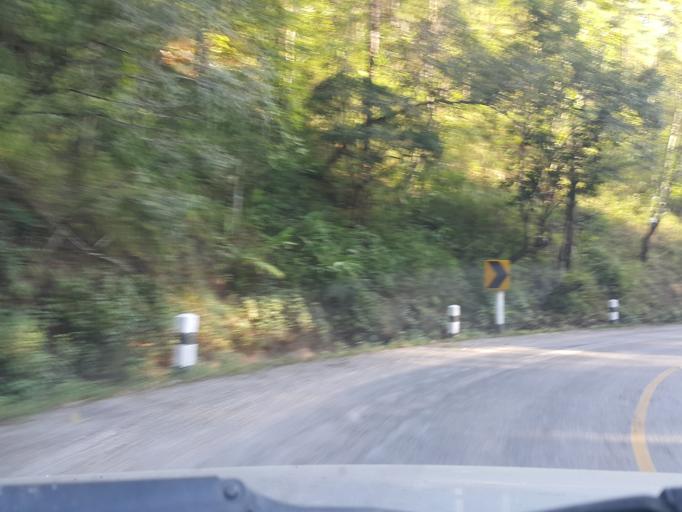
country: TH
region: Mae Hong Son
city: Mae Hi
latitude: 19.2617
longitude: 98.6382
